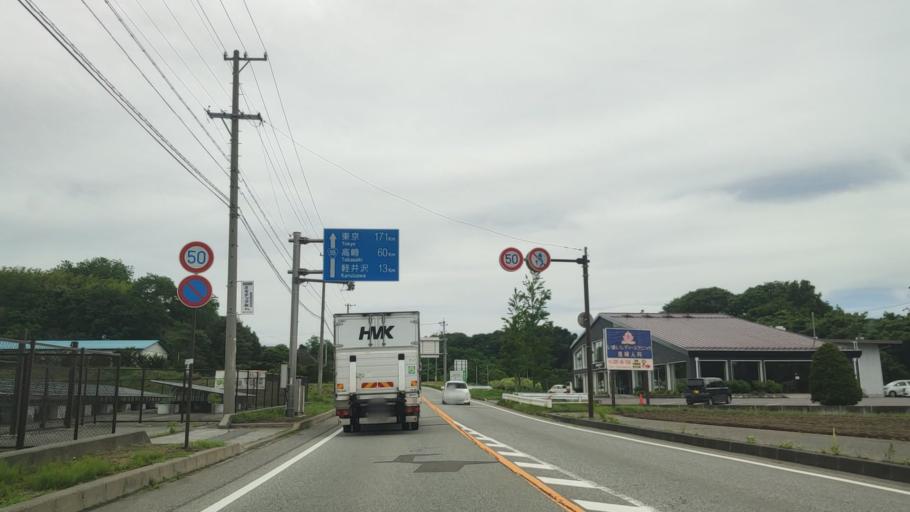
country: JP
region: Nagano
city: Komoro
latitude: 36.3142
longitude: 138.4596
